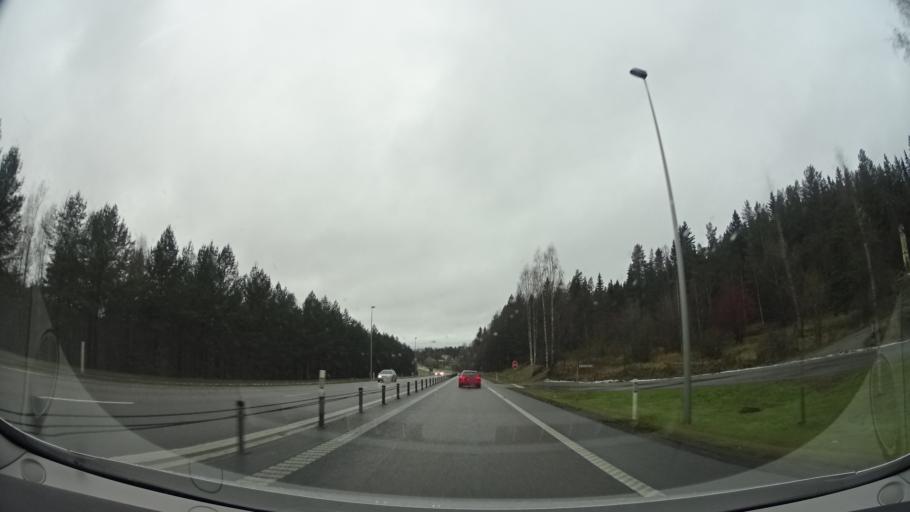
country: SE
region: Vaesterbotten
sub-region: Skelleftea Kommun
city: Skelleftea
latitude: 64.7615
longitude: 20.9920
